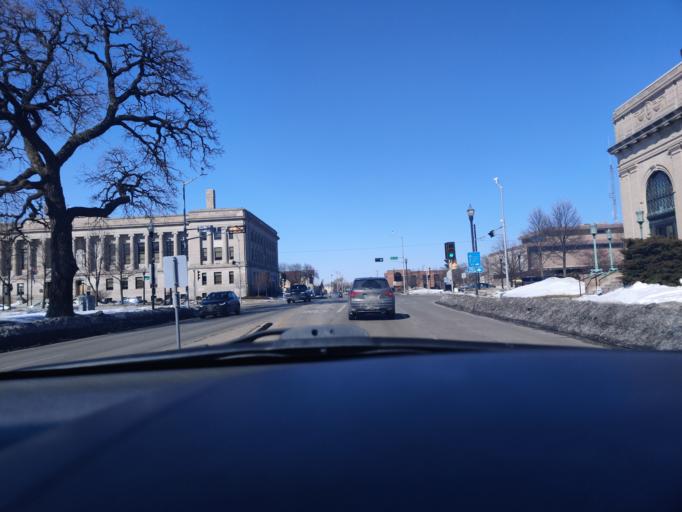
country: US
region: Wisconsin
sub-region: Kenosha County
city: Kenosha
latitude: 42.5841
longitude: -87.8221
